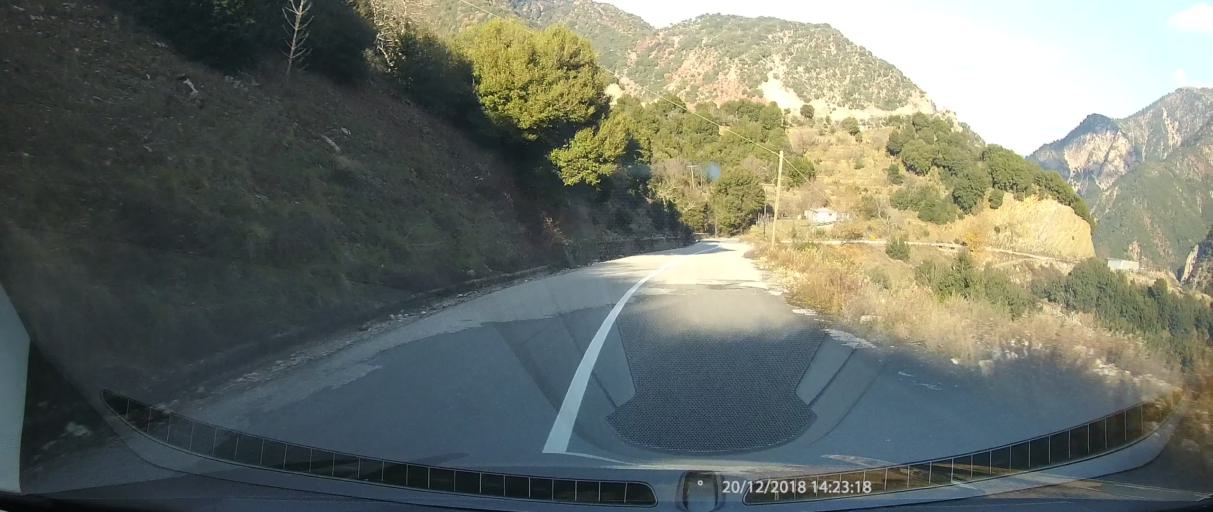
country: GR
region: West Greece
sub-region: Nomos Aitolias kai Akarnanias
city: Thermo
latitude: 38.7554
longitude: 21.6688
